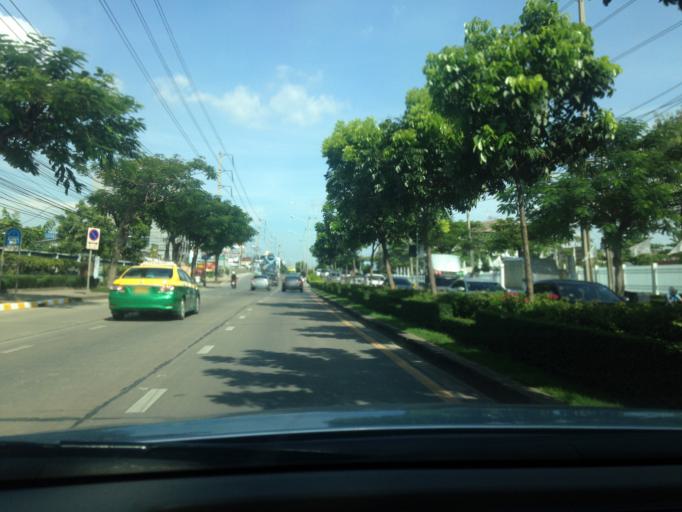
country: TH
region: Bangkok
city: Lat Krabang
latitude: 13.7223
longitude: 100.7281
